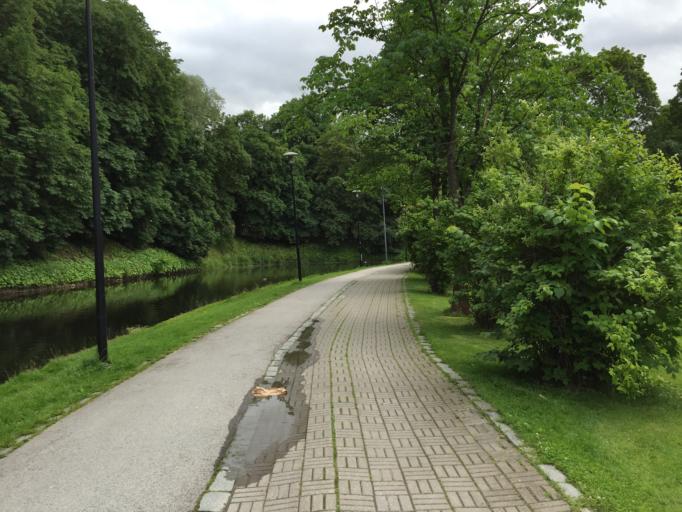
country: EE
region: Harju
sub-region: Tallinna linn
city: Tallinn
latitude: 59.4372
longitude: 24.7351
